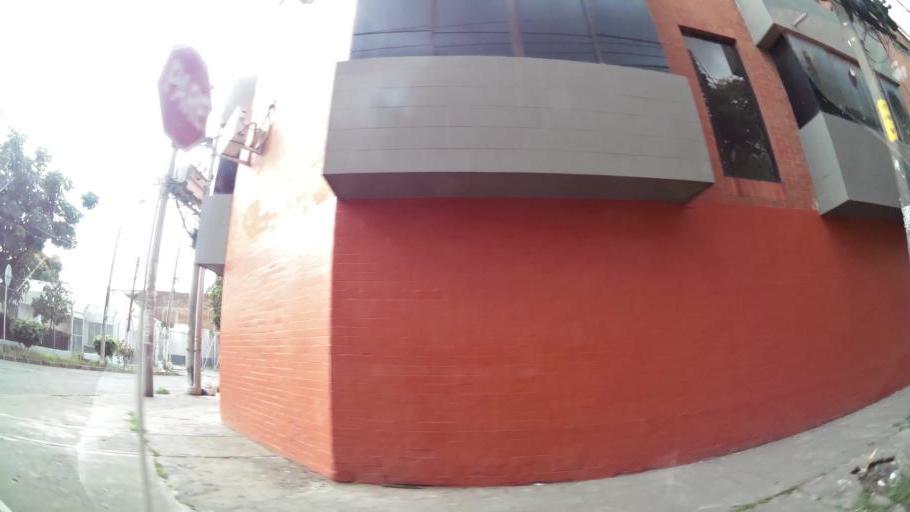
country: CO
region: Valle del Cauca
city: Cali
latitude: 3.4728
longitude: -76.5090
